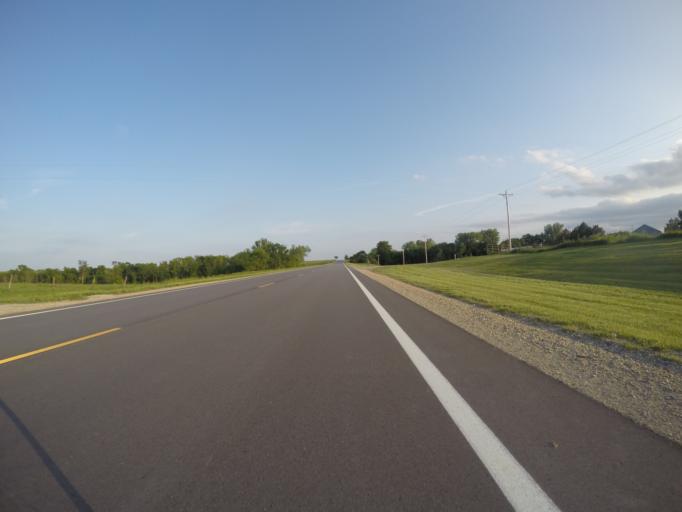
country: US
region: Kansas
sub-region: Pottawatomie County
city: Westmoreland
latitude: 39.3831
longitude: -96.5199
